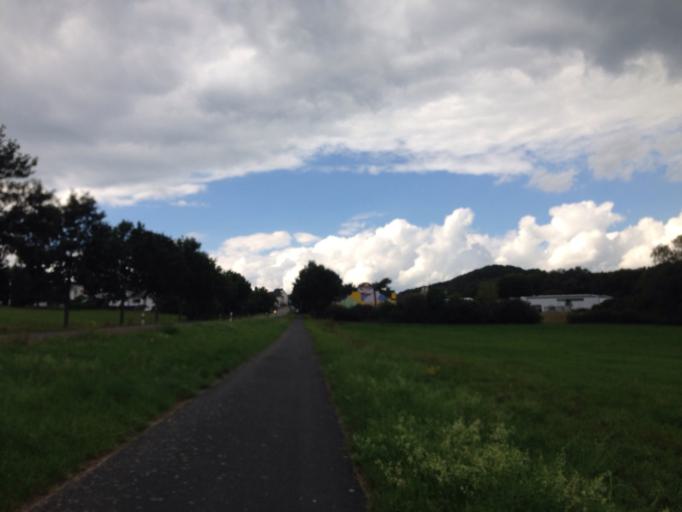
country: DE
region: Hesse
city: Mengerskirchen
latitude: 50.5476
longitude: 8.1855
